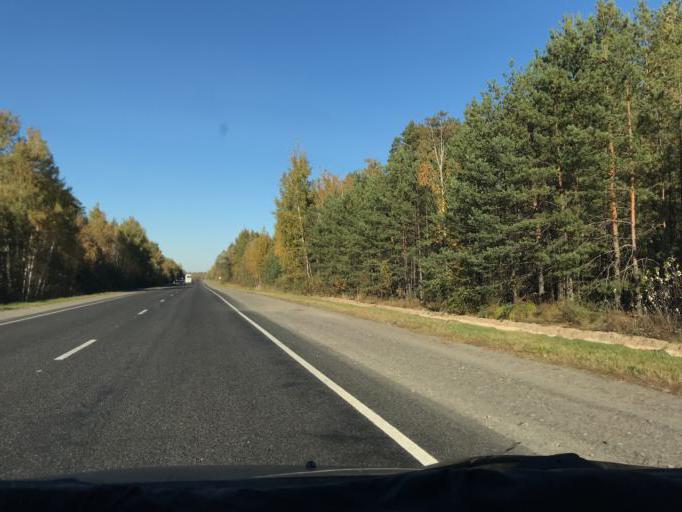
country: BY
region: Gomel
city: Kalinkavichy
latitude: 52.1003
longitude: 29.3675
